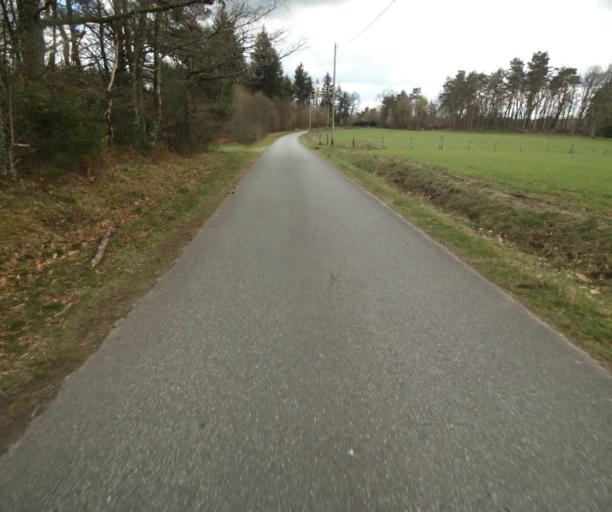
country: FR
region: Limousin
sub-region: Departement de la Correze
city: Correze
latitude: 45.3000
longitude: 1.9218
